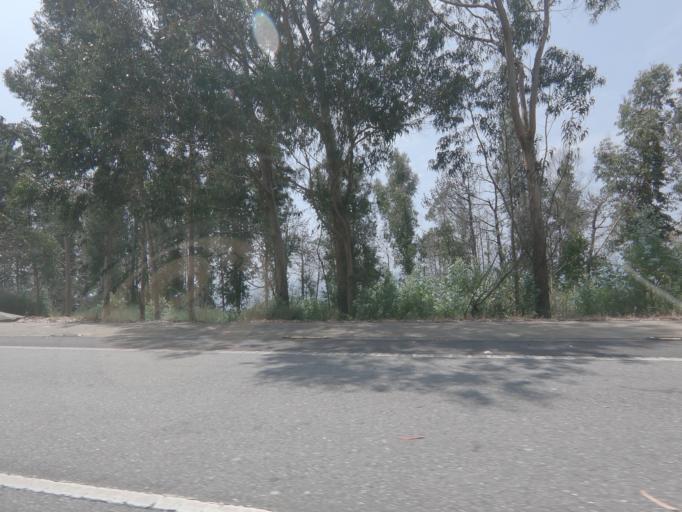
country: ES
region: Galicia
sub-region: Provincia de Pontevedra
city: A Guarda
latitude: 41.9241
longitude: -8.8807
